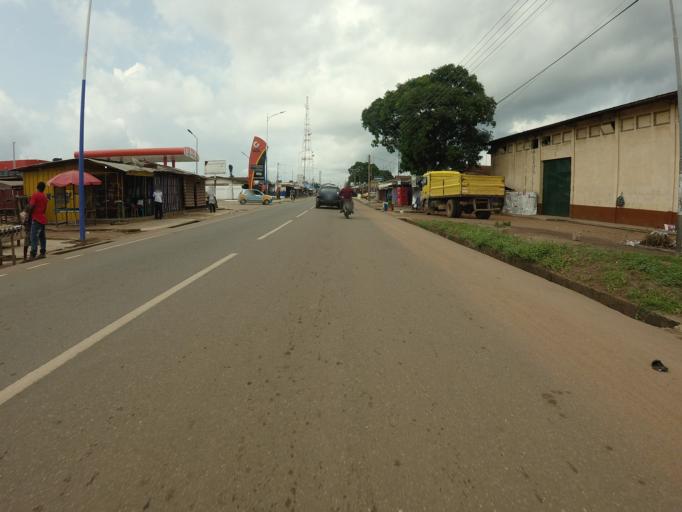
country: GH
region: Volta
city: Hohoe
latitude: 7.1508
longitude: 0.4720
